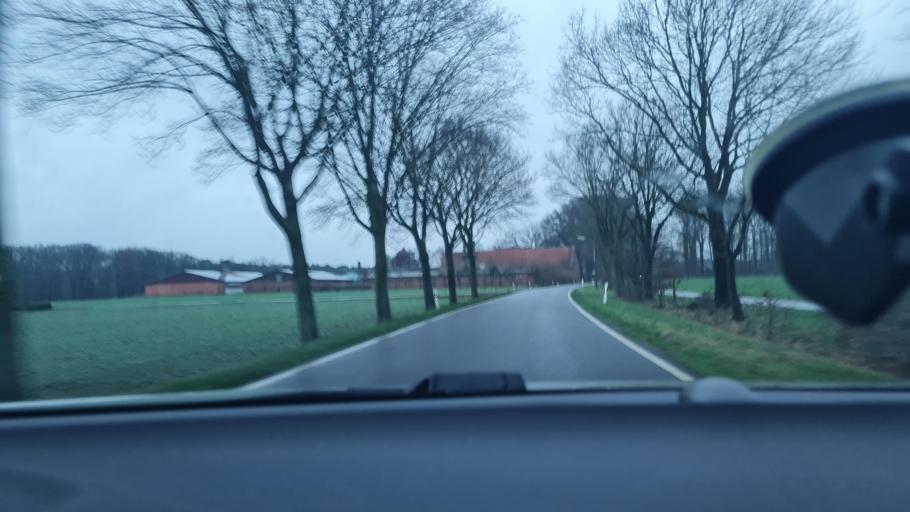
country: DE
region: North Rhine-Westphalia
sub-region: Regierungsbezirk Munster
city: Heiden
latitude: 51.7673
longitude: 6.9285
